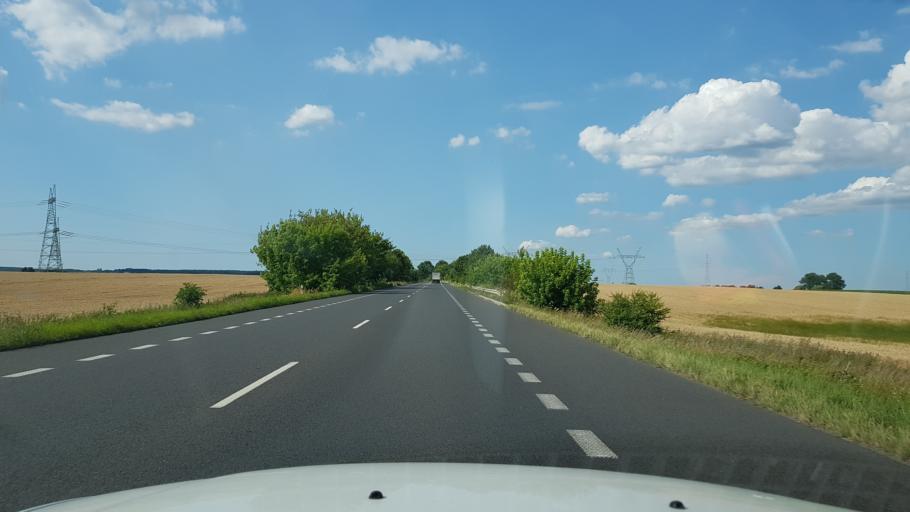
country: PL
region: West Pomeranian Voivodeship
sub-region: Powiat gryfinski
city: Stare Czarnowo
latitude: 53.2611
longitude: 14.7844
